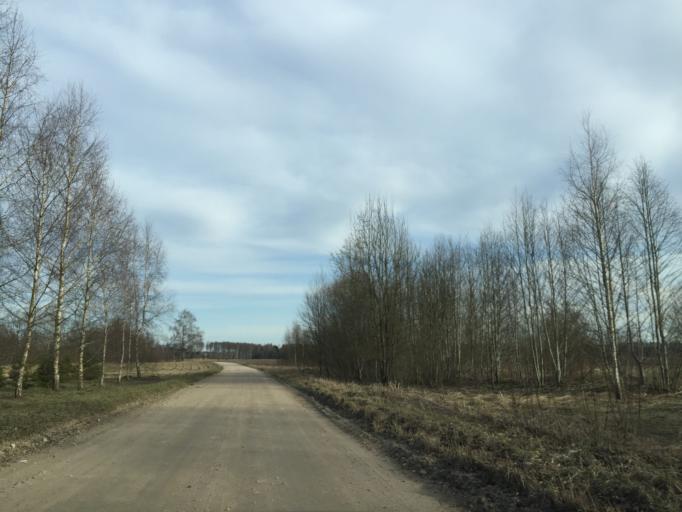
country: LV
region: Kegums
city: Kegums
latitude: 56.7983
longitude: 24.7497
